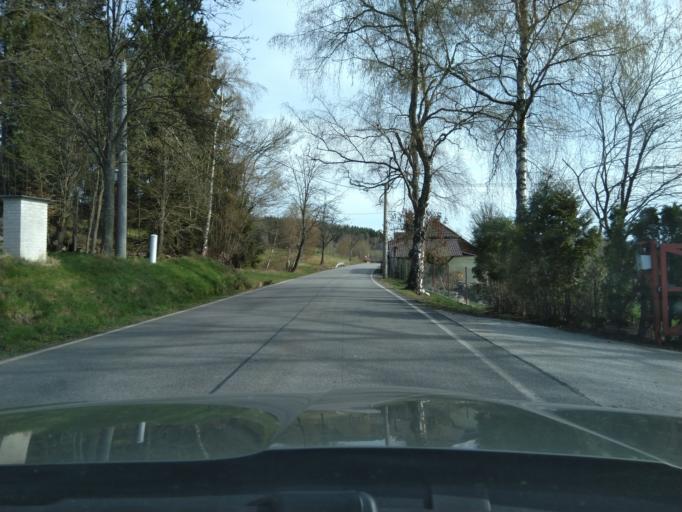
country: CZ
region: Jihocesky
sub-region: Okres Prachatice
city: Stachy
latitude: 49.0839
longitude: 13.6408
